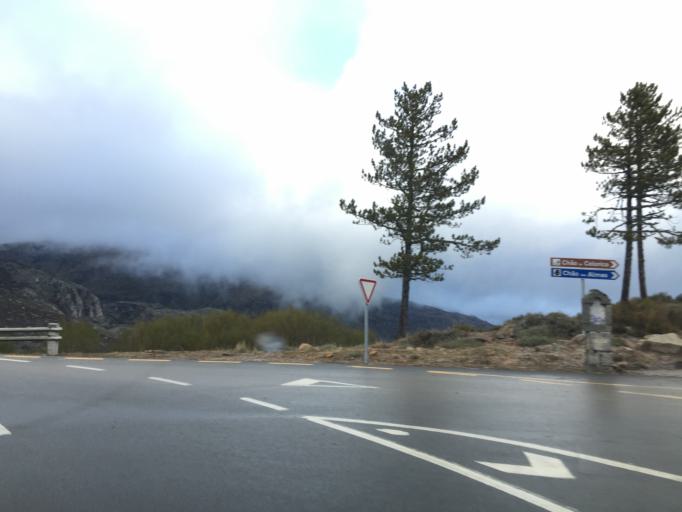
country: PT
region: Castelo Branco
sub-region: Covilha
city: Covilha
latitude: 40.3267
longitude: -7.5706
